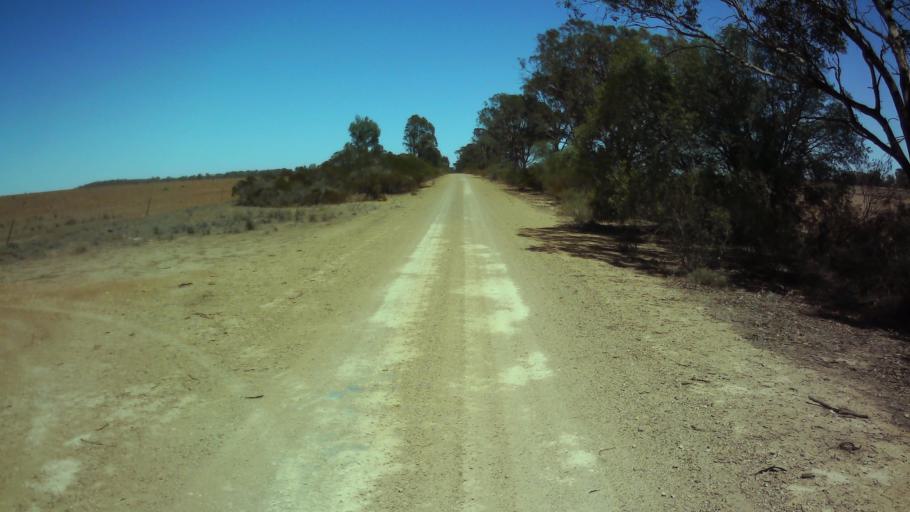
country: AU
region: New South Wales
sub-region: Forbes
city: Forbes
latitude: -33.6941
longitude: 147.8227
